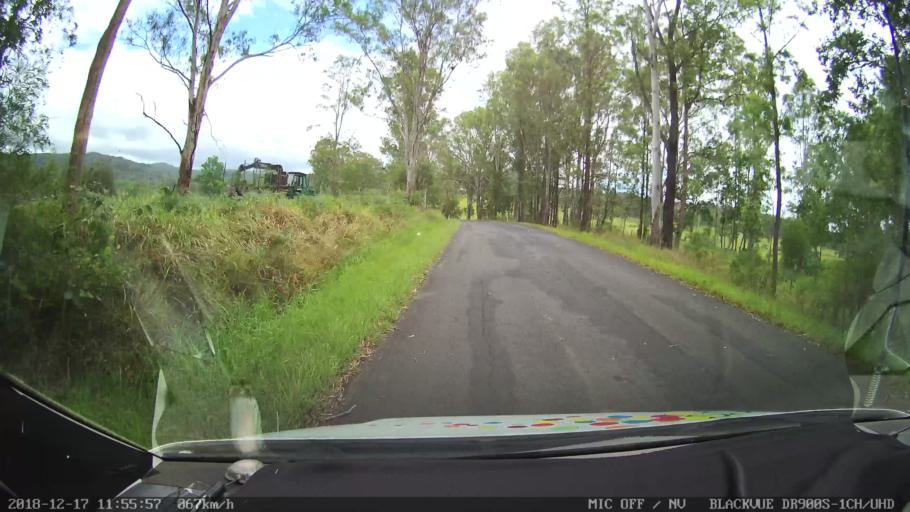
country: AU
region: New South Wales
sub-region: Kyogle
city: Kyogle
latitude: -28.5513
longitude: 152.5822
